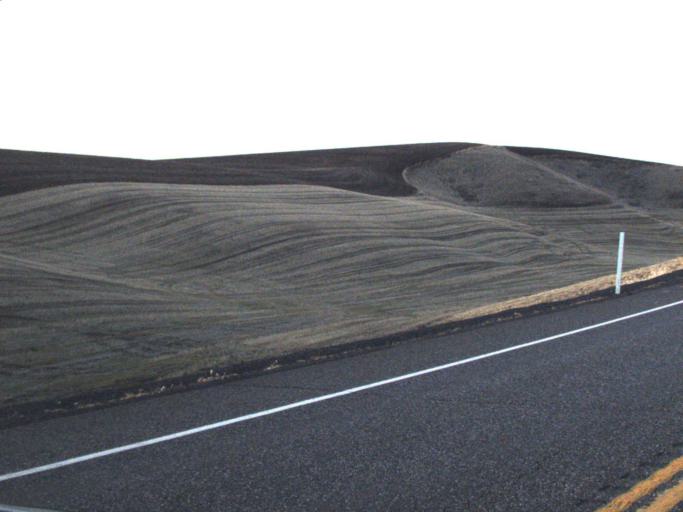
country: US
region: Washington
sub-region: Garfield County
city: Pomeroy
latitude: 46.7266
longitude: -117.7635
